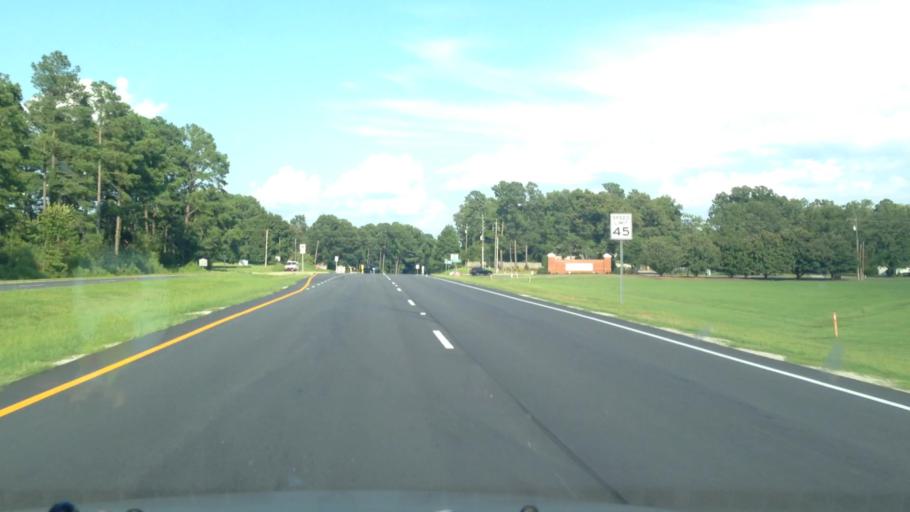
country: US
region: North Carolina
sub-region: Harnett County
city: Buies Creek
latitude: 35.4073
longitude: -78.7544
